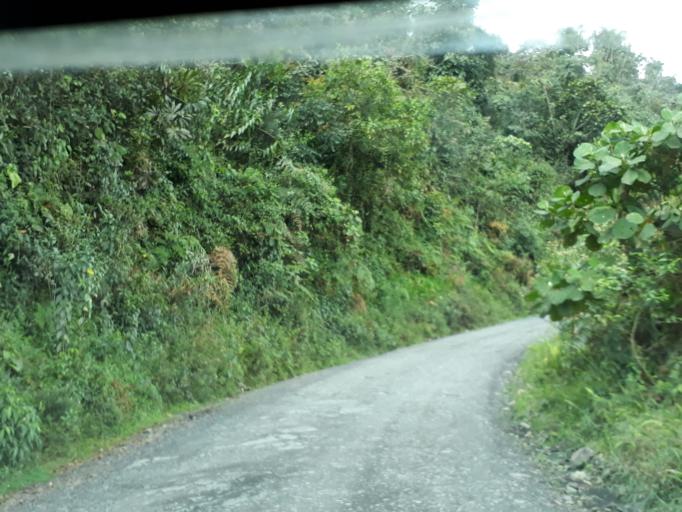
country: CO
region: Cundinamarca
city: Pacho
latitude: 5.2572
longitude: -74.1800
